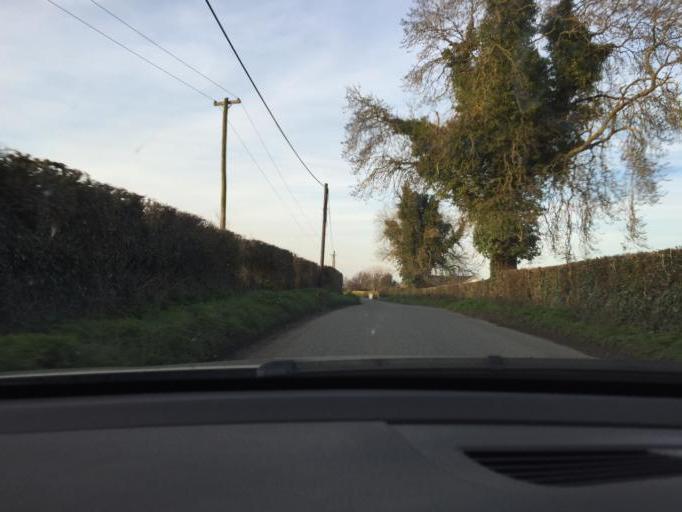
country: IE
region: Leinster
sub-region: An Mhi
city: Dunboyne
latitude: 53.4428
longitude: -6.4417
